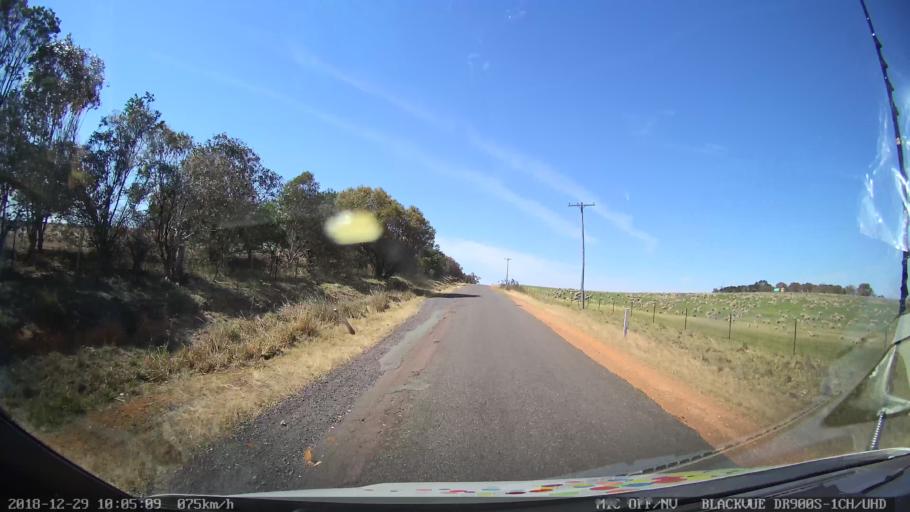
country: AU
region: New South Wales
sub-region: Goulburn Mulwaree
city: Goulburn
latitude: -34.8302
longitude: 149.4536
